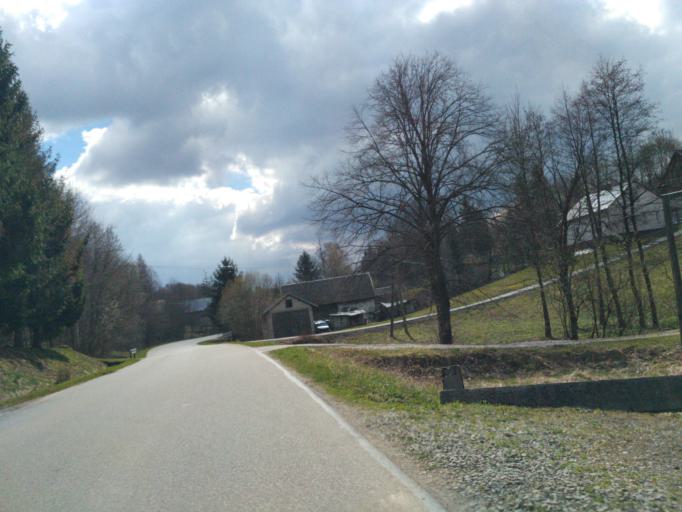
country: PL
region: Subcarpathian Voivodeship
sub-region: Powiat brzozowski
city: Dydnia
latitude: 49.6609
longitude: 22.1981
